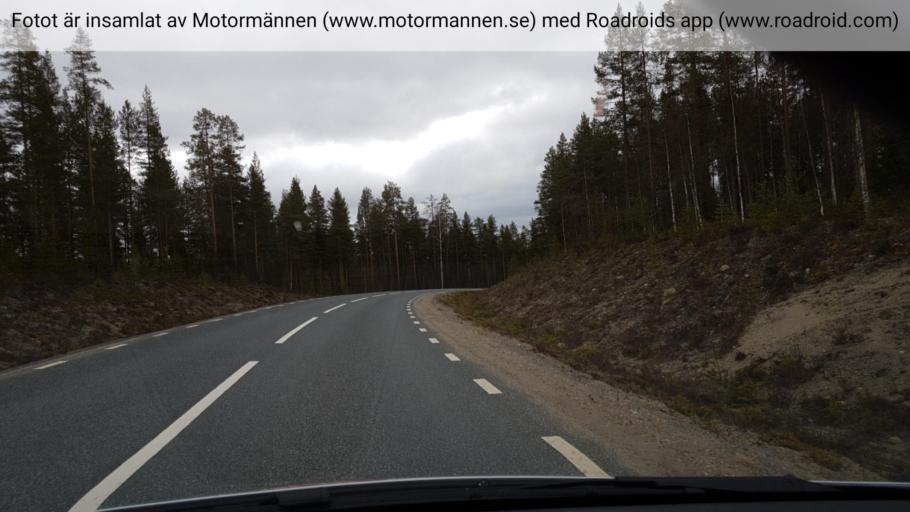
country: SE
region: Vaesternorrland
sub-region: OErnskoeldsviks Kommun
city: Bredbyn
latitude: 63.8166
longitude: 18.4825
